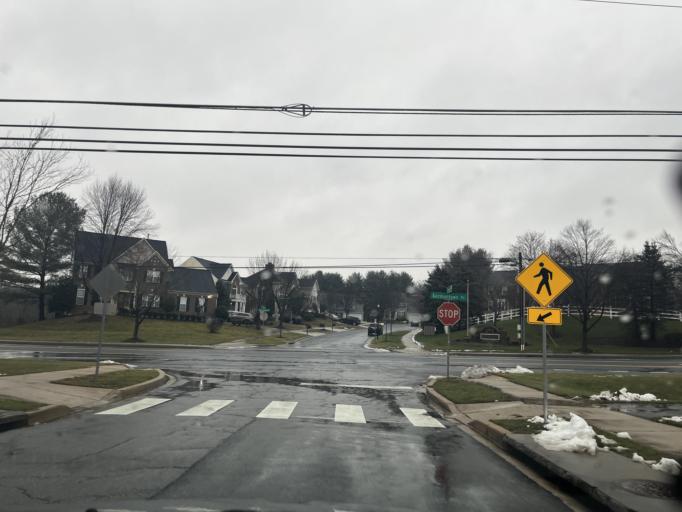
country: US
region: Maryland
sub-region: Montgomery County
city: Germantown
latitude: 39.1571
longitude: -77.2858
